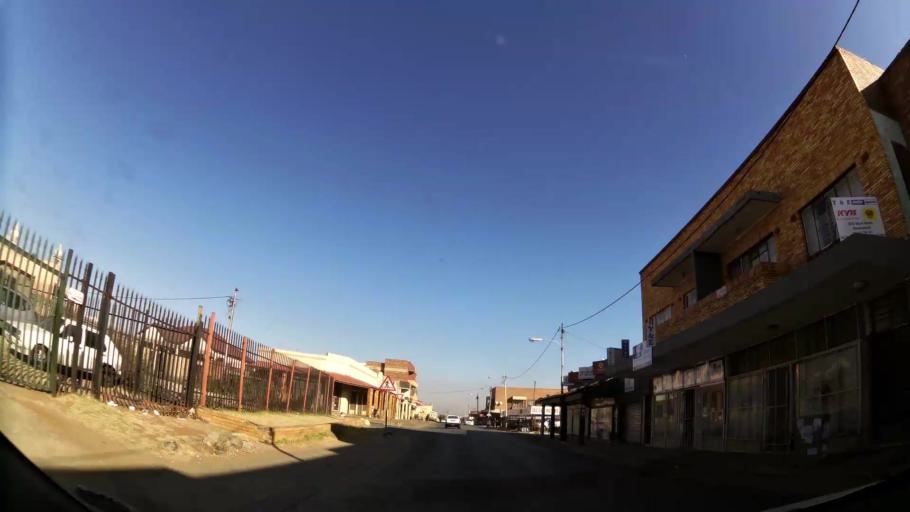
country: ZA
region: Gauteng
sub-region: City of Johannesburg Metropolitan Municipality
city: Roodepoort
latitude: -26.1627
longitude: 27.8646
